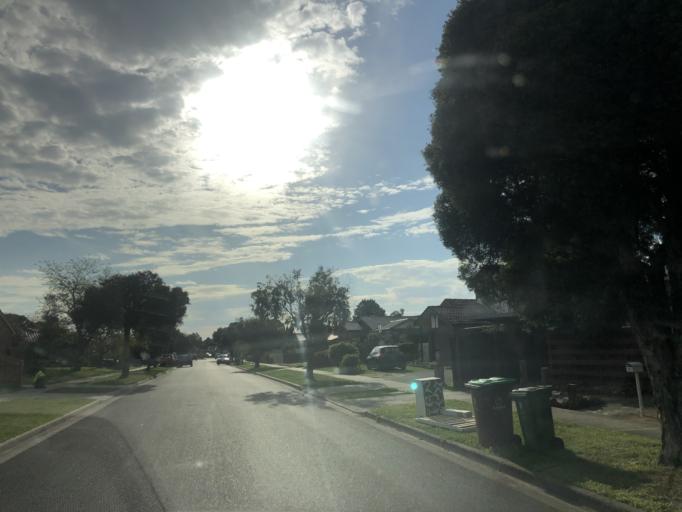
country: AU
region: Victoria
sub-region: Casey
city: Hallam
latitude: -38.0264
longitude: 145.2602
